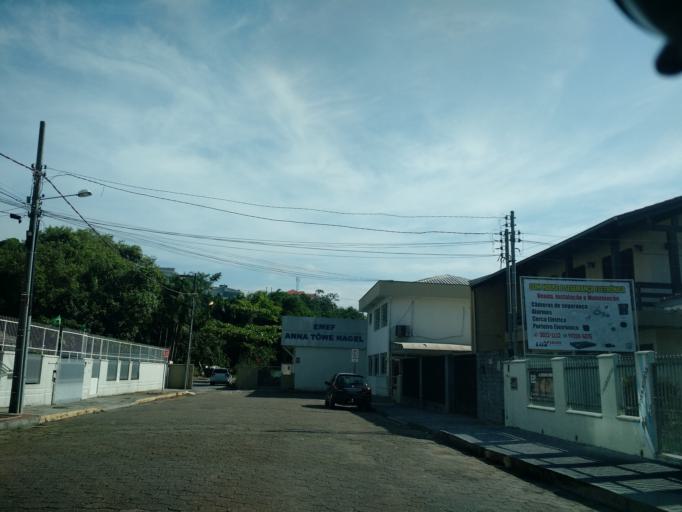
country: BR
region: Santa Catarina
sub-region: Jaragua Do Sul
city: Jaragua do Sul
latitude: -26.4789
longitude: -49.1065
